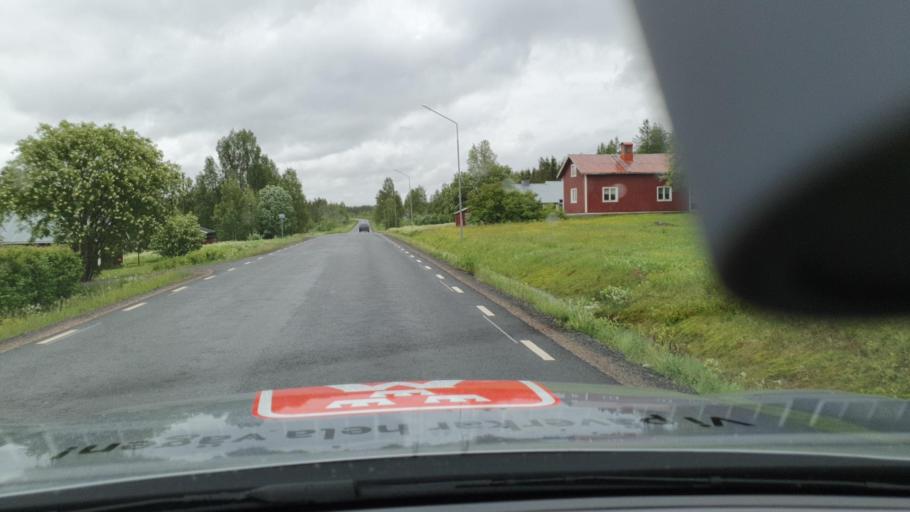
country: FI
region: Lapland
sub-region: Torniolaakso
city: Ylitornio
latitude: 66.1690
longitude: 23.8228
